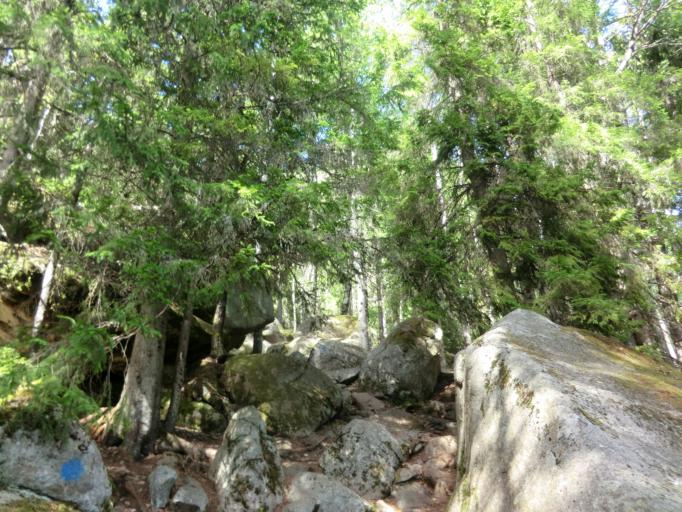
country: SE
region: Vaesternorrland
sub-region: Kramfors Kommun
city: Nordingra
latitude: 63.0728
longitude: 18.3518
